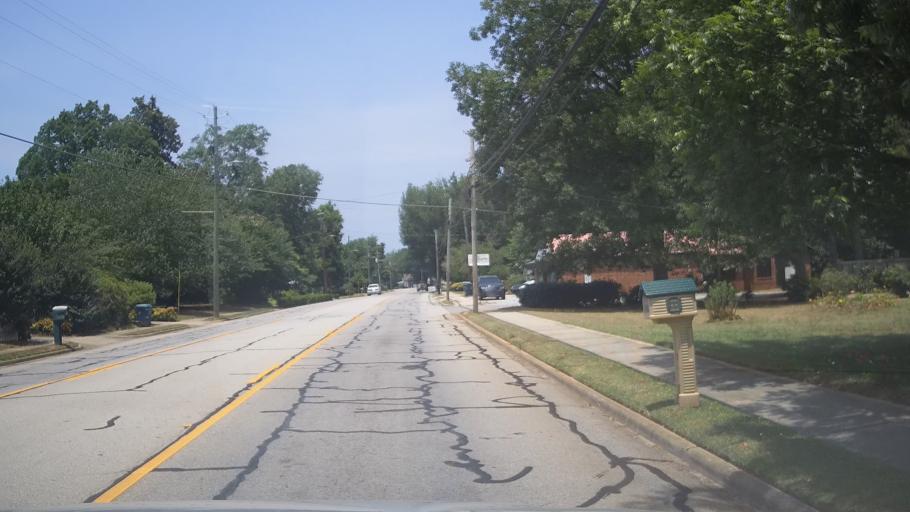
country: US
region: Georgia
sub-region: Hart County
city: Hartwell
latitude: 34.3451
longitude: -82.9258
